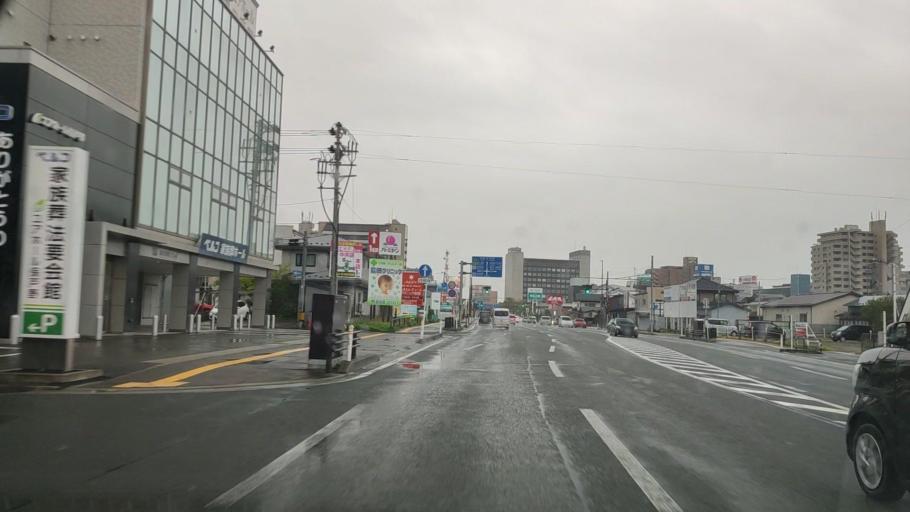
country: JP
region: Akita
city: Akita Shi
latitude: 39.7230
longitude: 140.1090
